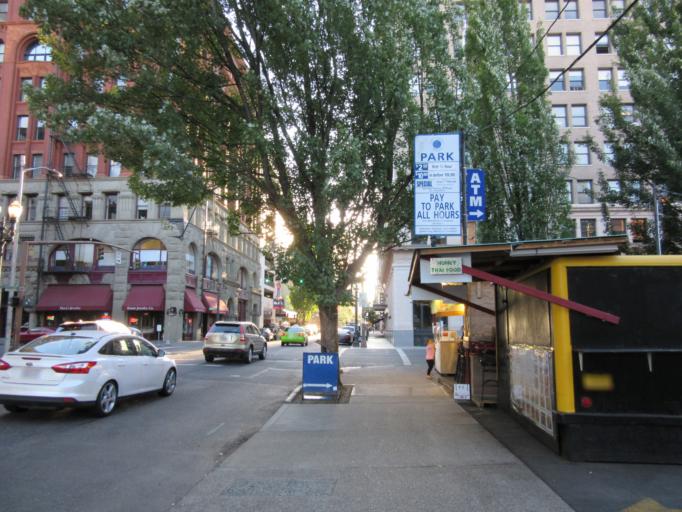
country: US
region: Oregon
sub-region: Multnomah County
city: Portland
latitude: 45.5196
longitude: -122.6745
